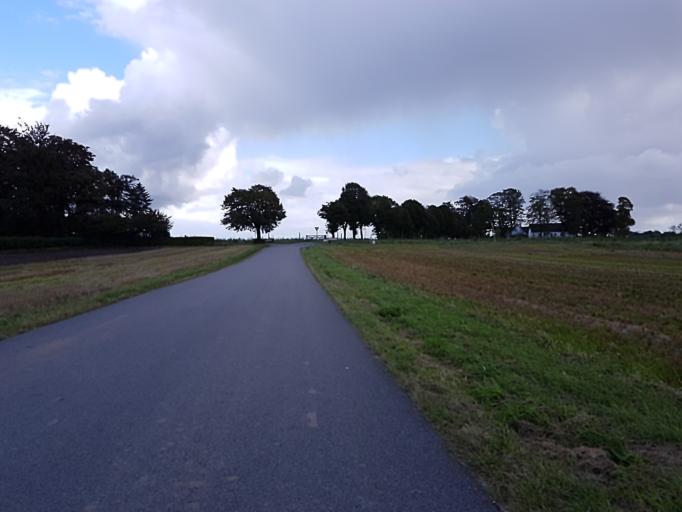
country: DK
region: Zealand
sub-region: Roskilde Kommune
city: Gundsomagle
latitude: 55.7209
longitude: 12.1893
